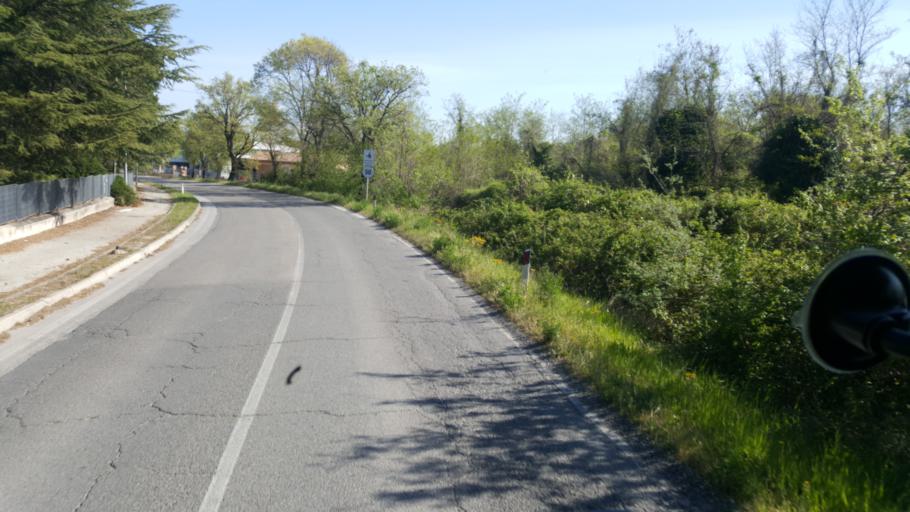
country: IT
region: Emilia-Romagna
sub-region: Provincia di Rimini
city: Torriana
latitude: 43.9951
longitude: 12.4023
